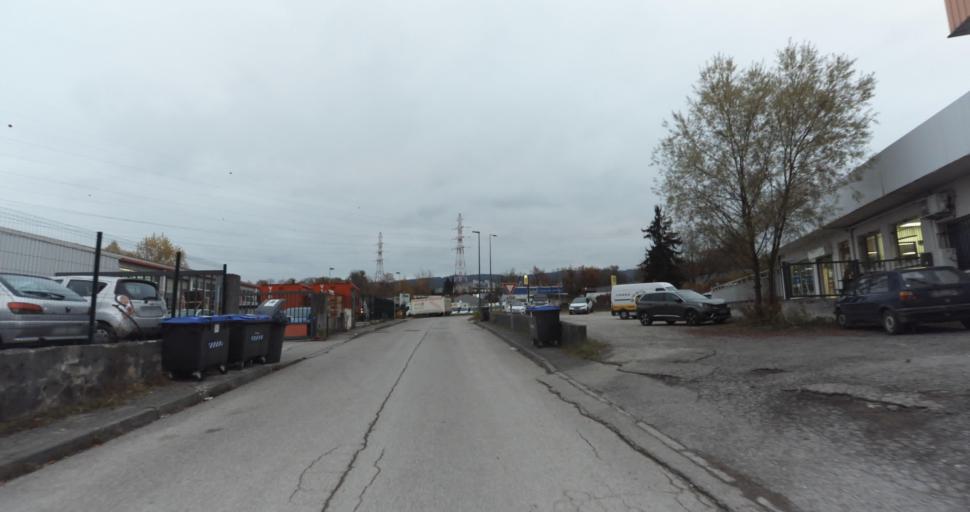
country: FR
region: Rhone-Alpes
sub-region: Departement de la Haute-Savoie
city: Seynod
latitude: 45.8900
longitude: 6.0806
